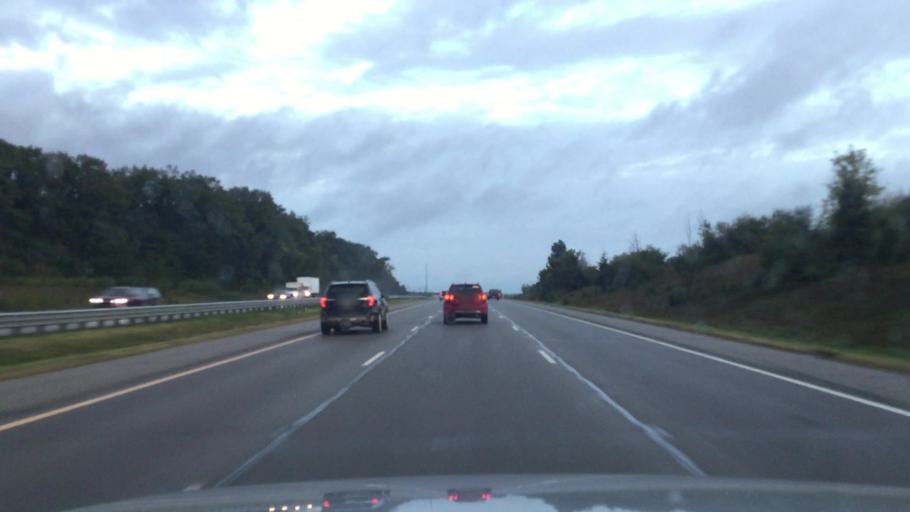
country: US
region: Michigan
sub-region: Oakland County
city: Holly
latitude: 42.8473
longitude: -83.5871
